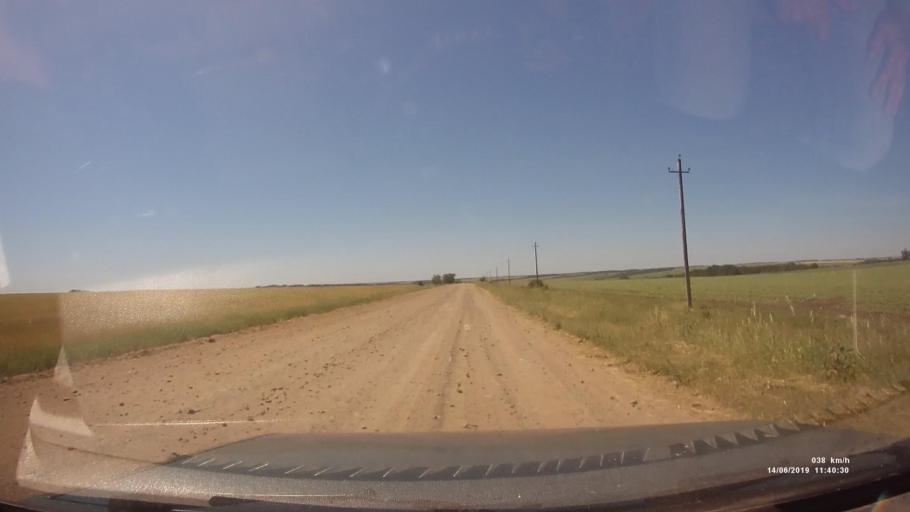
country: RU
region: Rostov
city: Kazanskaya
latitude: 49.8668
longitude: 41.3596
